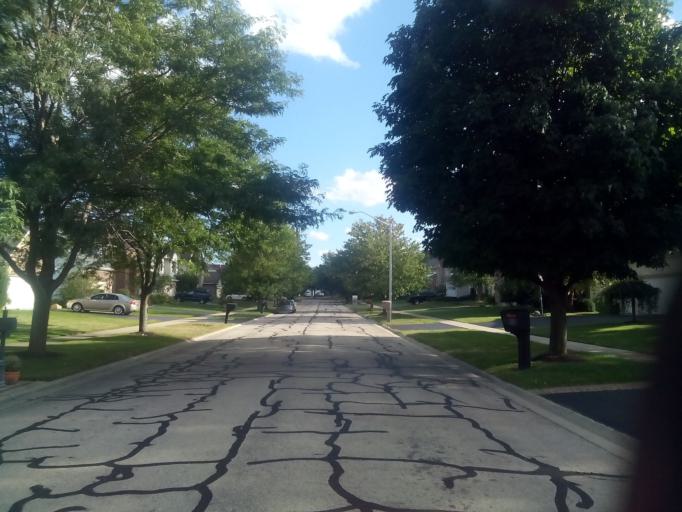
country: US
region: Illinois
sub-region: Will County
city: Romeoville
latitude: 41.6975
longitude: -88.1526
